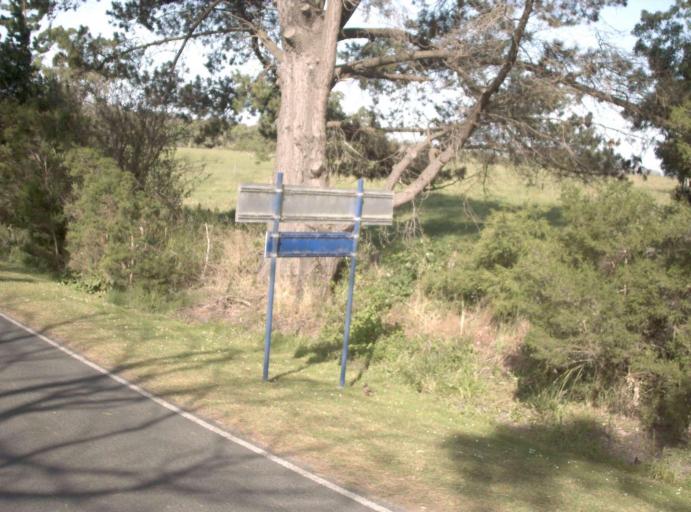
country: AU
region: Victoria
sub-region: Bass Coast
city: North Wonthaggi
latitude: -38.5728
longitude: 146.0218
